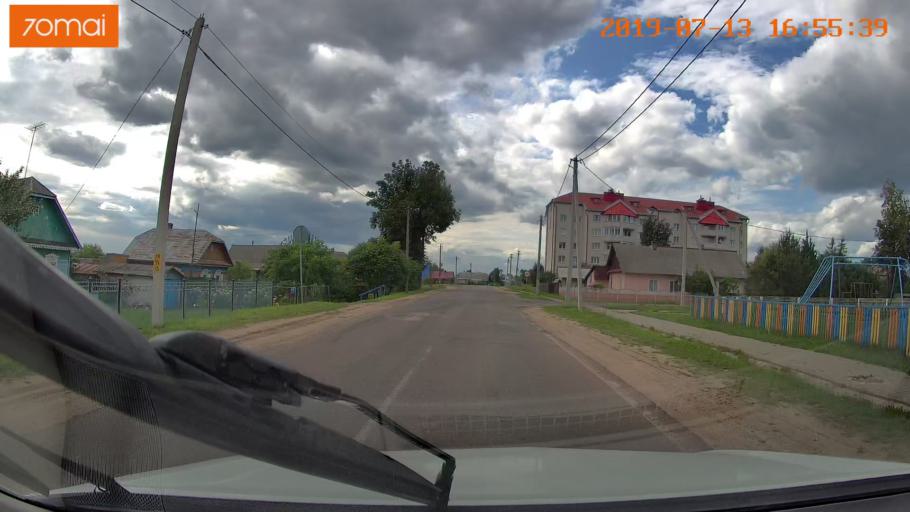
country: BY
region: Mogilev
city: Kirawsk
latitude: 53.2687
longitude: 29.4653
